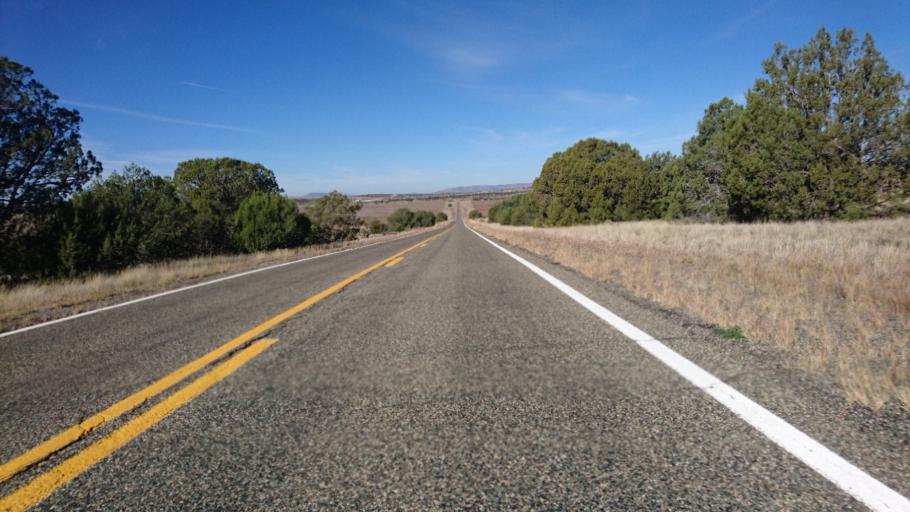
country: US
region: Arizona
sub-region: Yavapai County
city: Paulden
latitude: 35.2826
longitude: -112.7127
